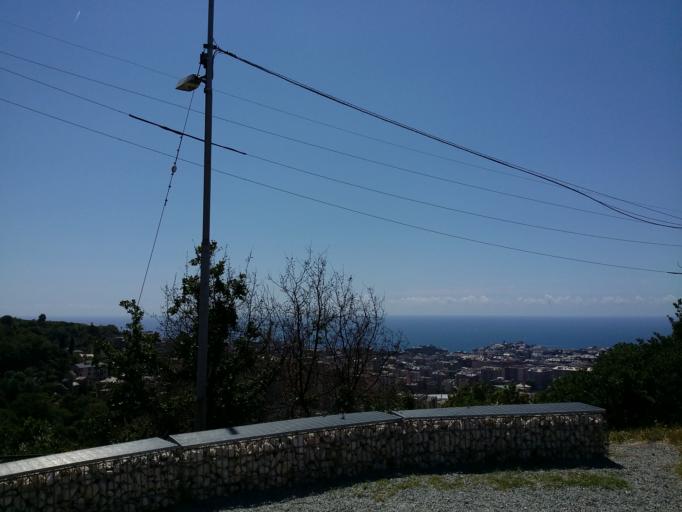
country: IT
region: Liguria
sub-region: Provincia di Genova
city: Genoa
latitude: 44.4136
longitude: 8.9787
